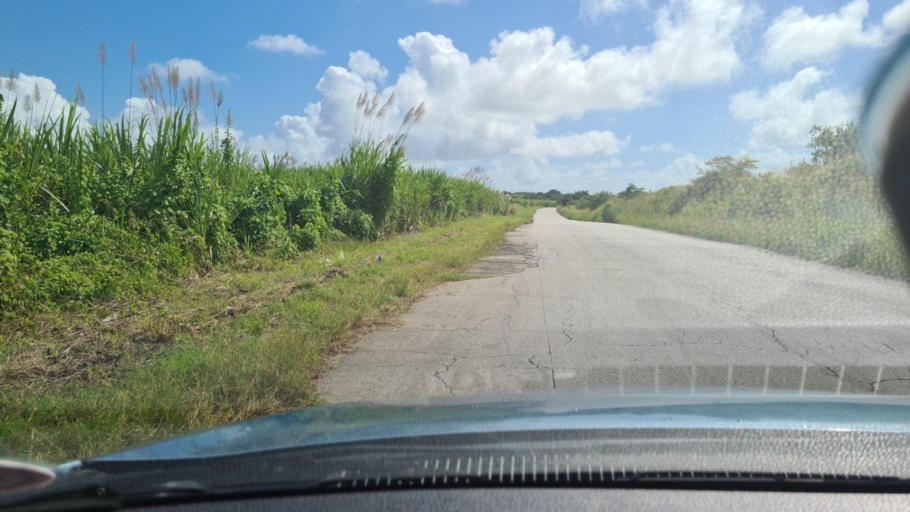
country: BB
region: Christ Church
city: Oistins
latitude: 13.0865
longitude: -59.5399
